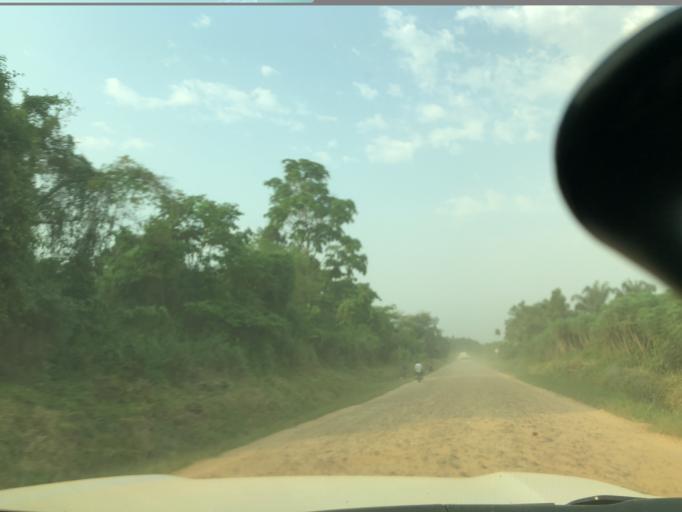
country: UG
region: Western Region
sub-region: Kasese District
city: Margherita
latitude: 0.3049
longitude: 29.6659
